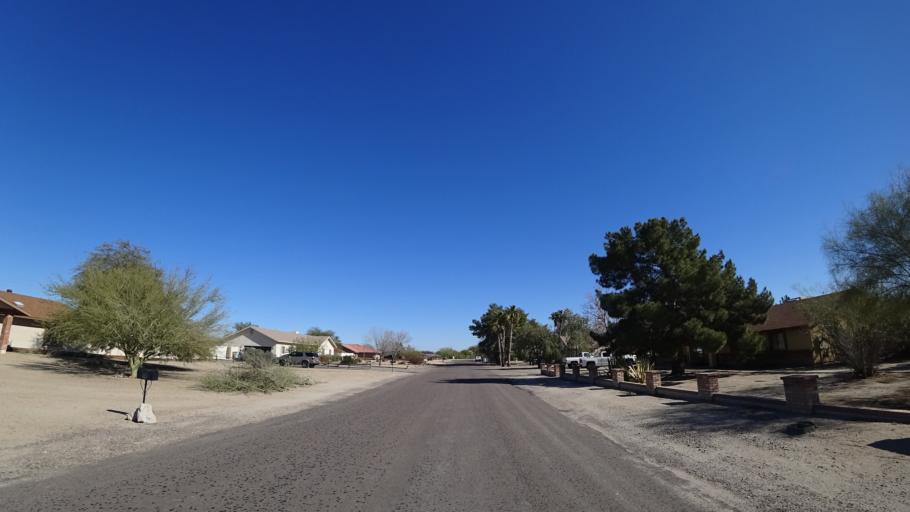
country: US
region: Arizona
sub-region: Maricopa County
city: Buckeye
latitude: 33.4277
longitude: -112.5236
